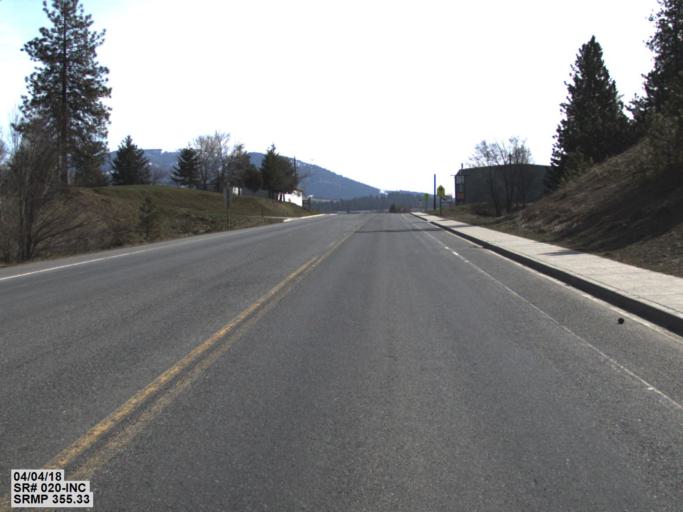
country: US
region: Washington
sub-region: Stevens County
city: Colville
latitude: 48.5470
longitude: -117.8846
